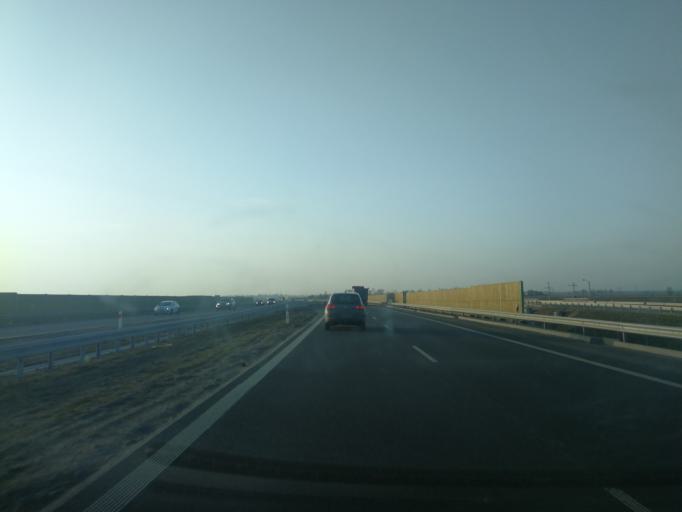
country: PL
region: Pomeranian Voivodeship
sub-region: Powiat nowodworski
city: Nowy Dwor Gdanski
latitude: 54.2342
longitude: 19.0393
